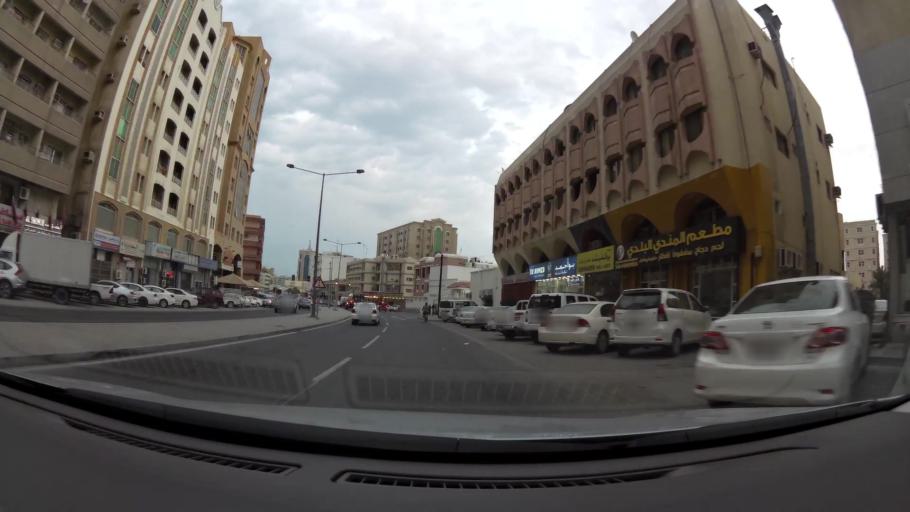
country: QA
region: Baladiyat ad Dawhah
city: Doha
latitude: 25.2744
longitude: 51.5224
